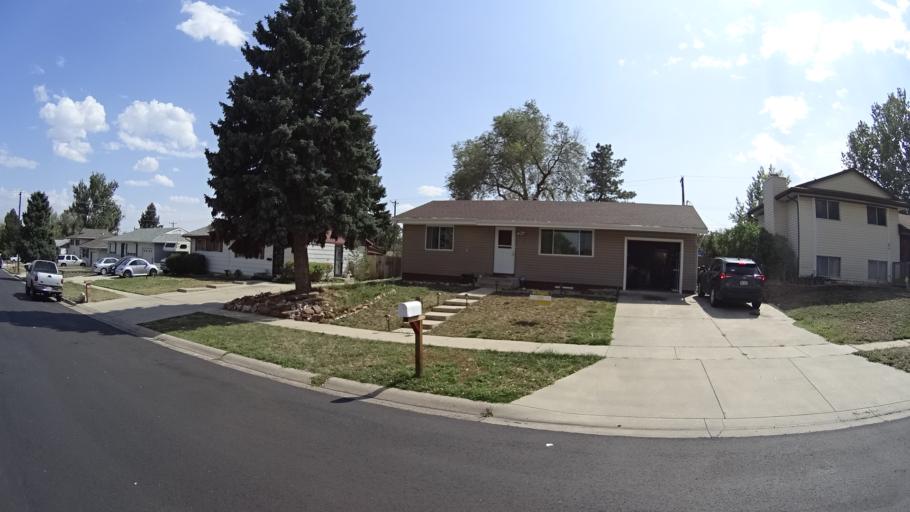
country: US
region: Colorado
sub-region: El Paso County
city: Colorado Springs
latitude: 38.8422
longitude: -104.7689
